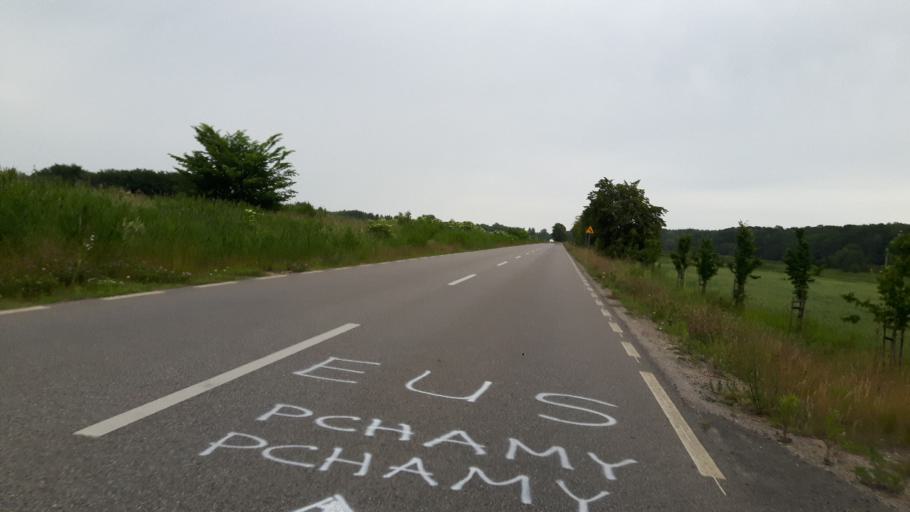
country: PL
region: Warmian-Masurian Voivodeship
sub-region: Powiat elblaski
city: Elblag
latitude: 54.2237
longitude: 19.3889
